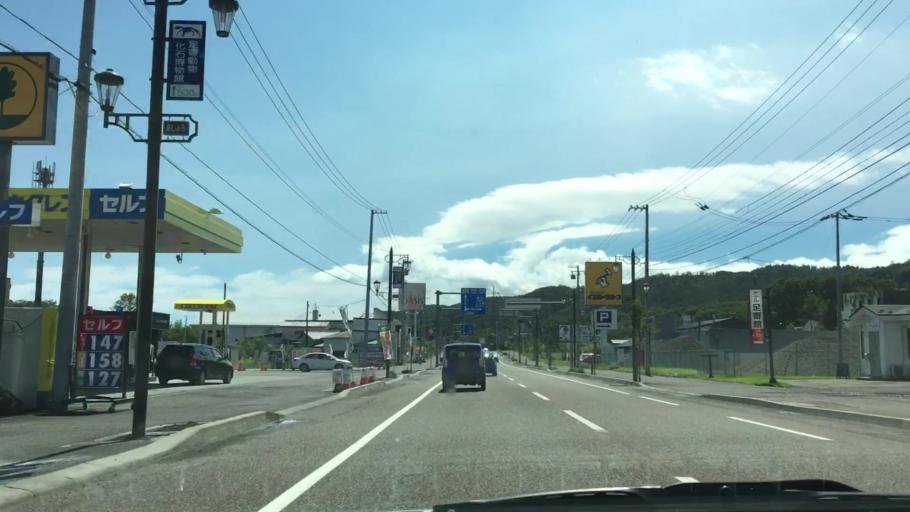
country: JP
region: Hokkaido
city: Otofuke
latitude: 43.2351
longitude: 143.5463
